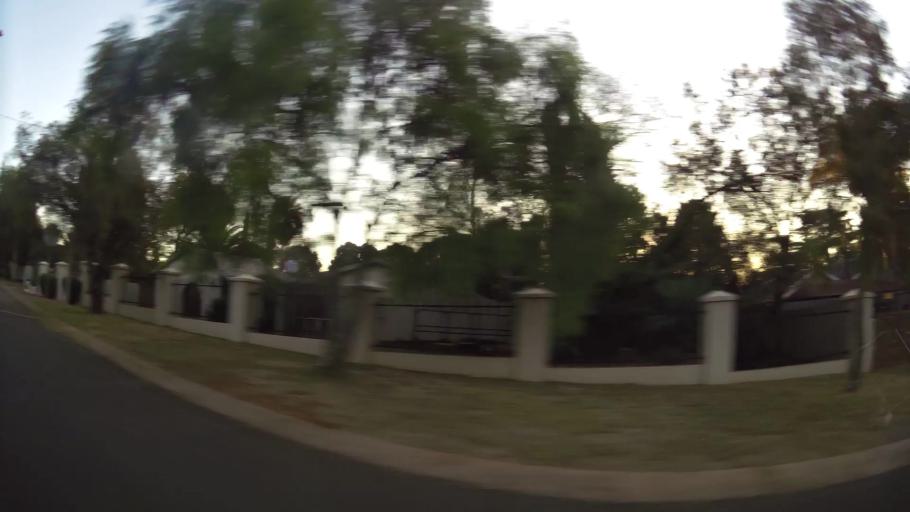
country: ZA
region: Gauteng
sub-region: City of Tshwane Metropolitan Municipality
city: Centurion
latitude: -25.8476
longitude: 28.1538
